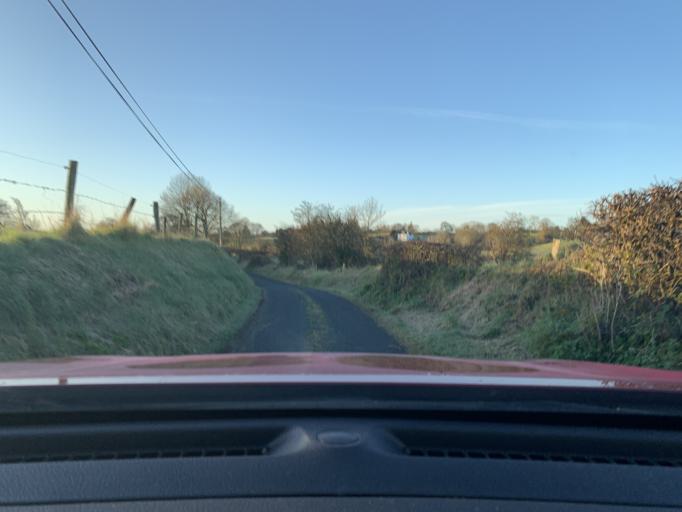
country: IE
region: Connaught
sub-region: Sligo
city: Ballymote
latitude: 54.0740
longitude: -8.5501
